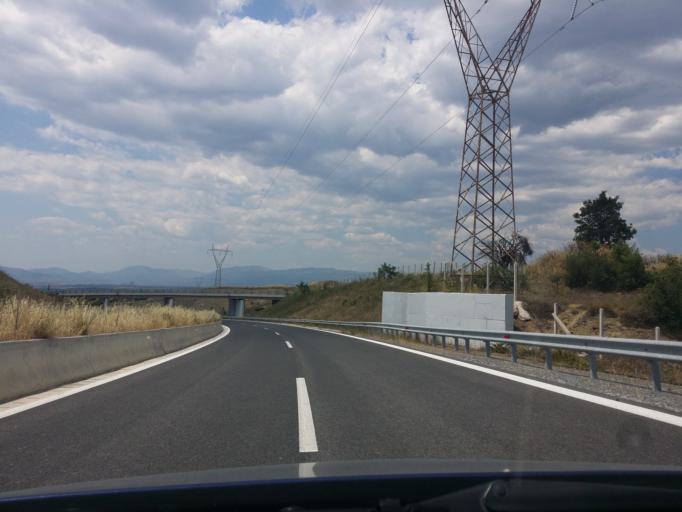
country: GR
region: Peloponnese
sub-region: Nomos Arkadias
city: Megalopoli
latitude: 37.3181
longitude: 22.1713
